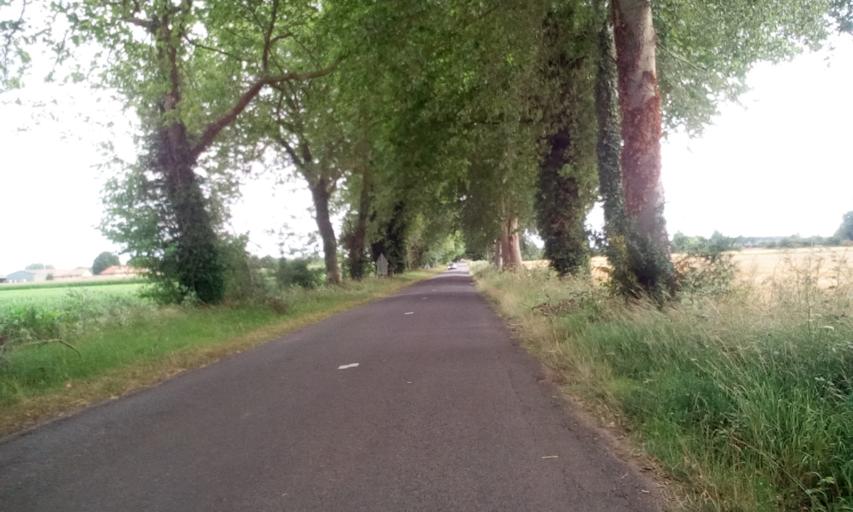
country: FR
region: Lower Normandy
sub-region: Departement du Calvados
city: Bellengreville
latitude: 49.1423
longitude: -0.2065
